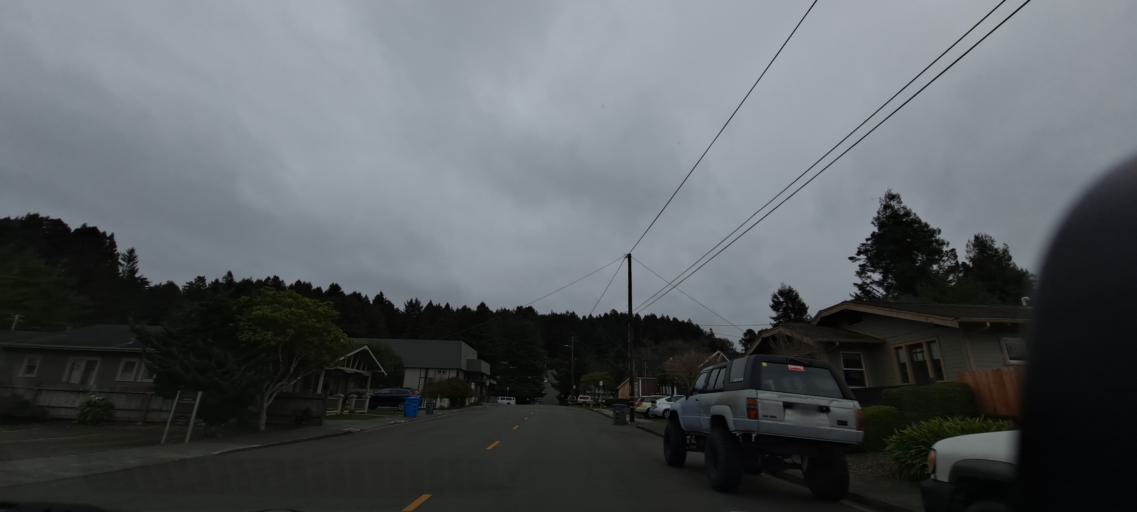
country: US
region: California
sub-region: Humboldt County
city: Arcata
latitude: 40.8708
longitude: -124.0791
